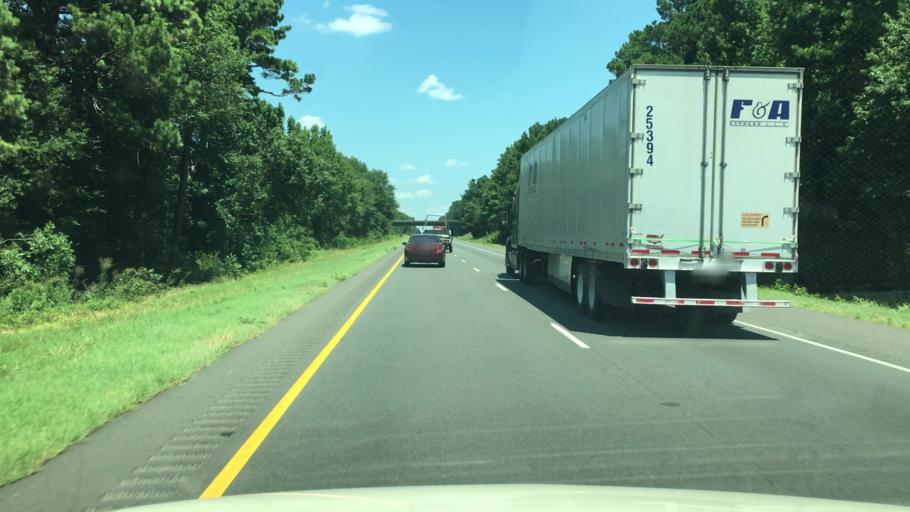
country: US
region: Arkansas
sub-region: Hempstead County
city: Hope
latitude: 33.7005
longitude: -93.5849
